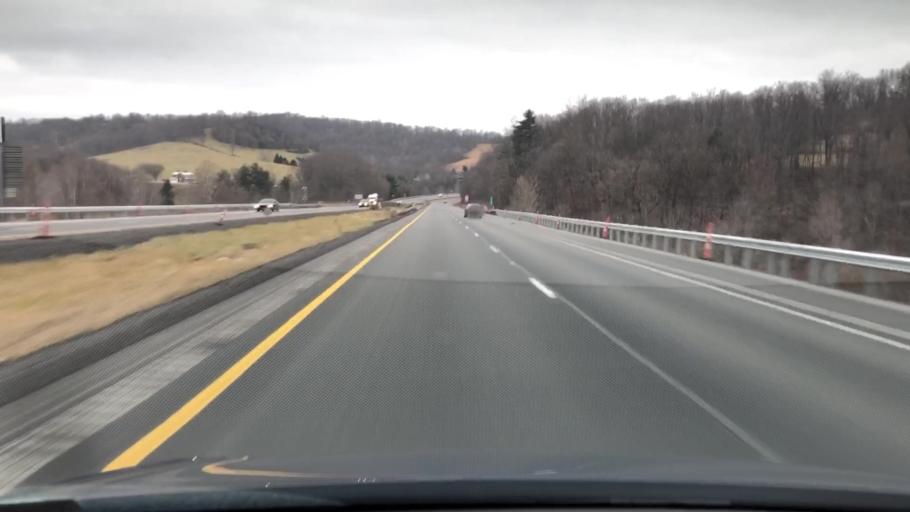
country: US
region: West Virginia
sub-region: Monongalia County
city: Star City
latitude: 39.7127
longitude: -80.0574
